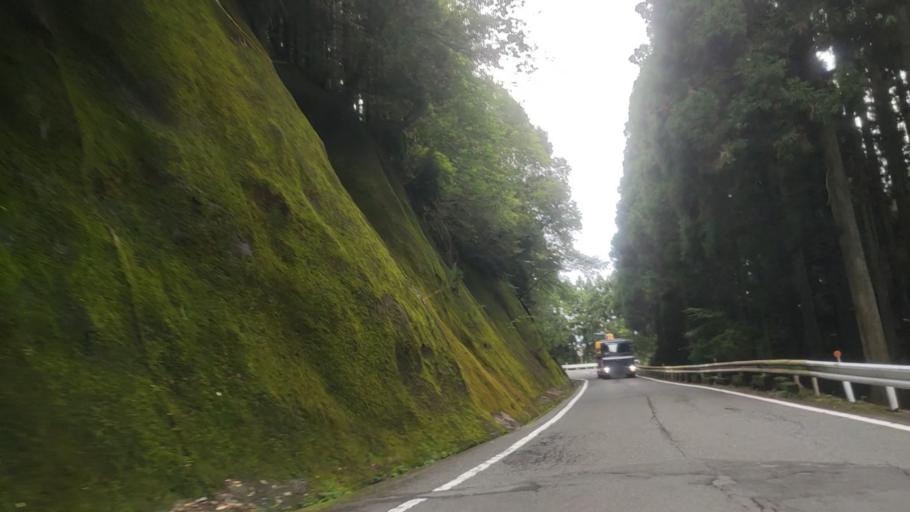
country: JP
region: Wakayama
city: Koya
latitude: 34.2105
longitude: 135.5431
